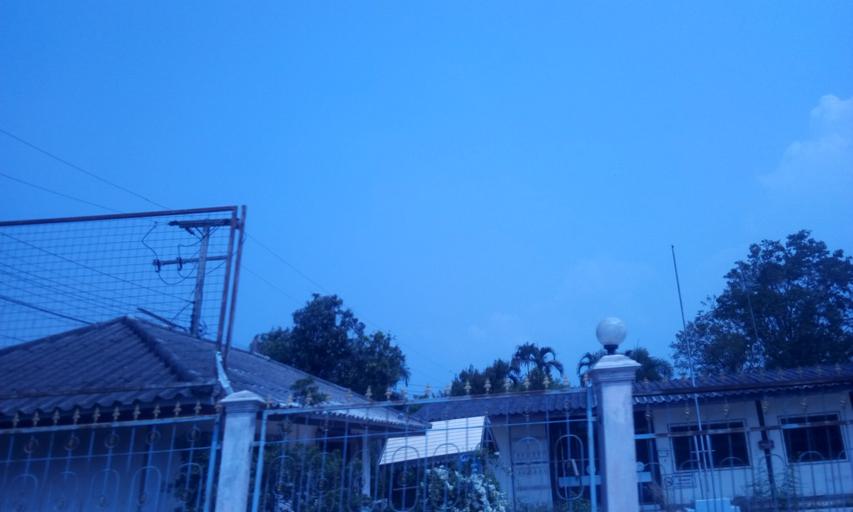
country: TH
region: Chon Buri
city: Phanat Nikhom
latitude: 13.4001
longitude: 101.1904
